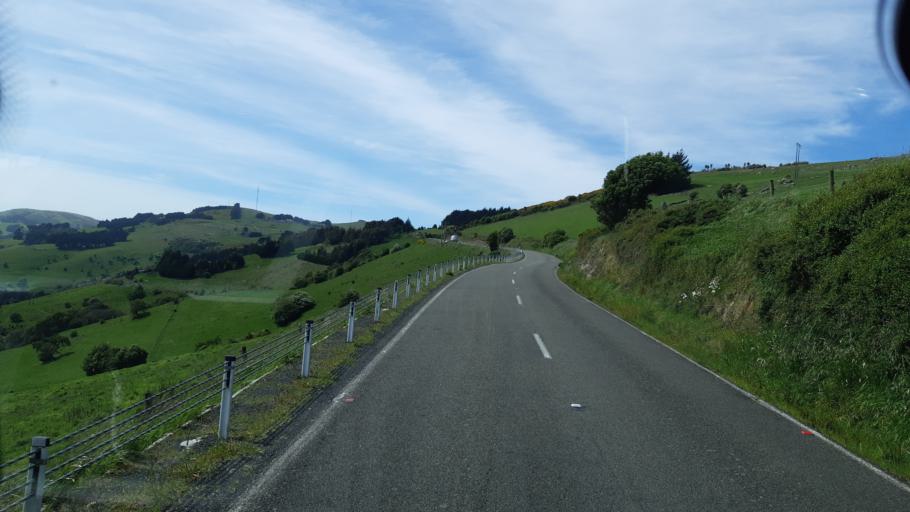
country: NZ
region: Otago
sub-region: Dunedin City
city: Dunedin
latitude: -45.8845
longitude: 170.5604
